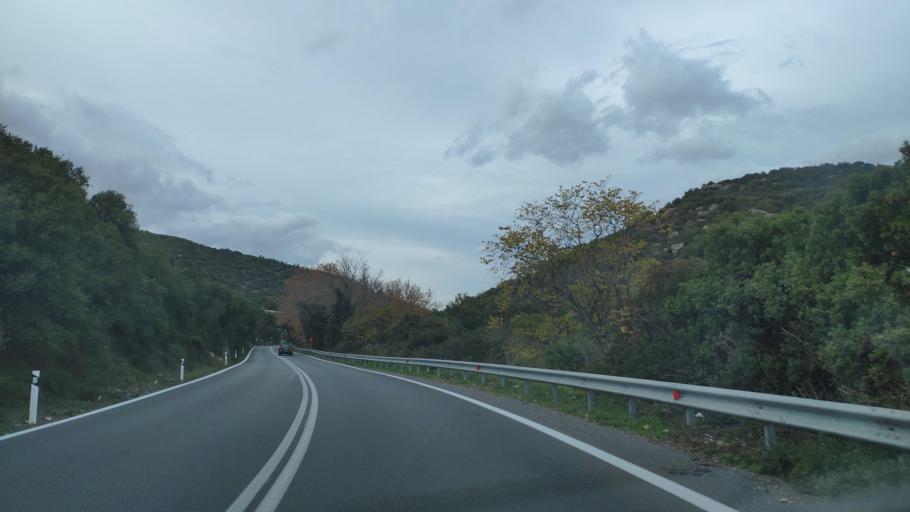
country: GR
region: Peloponnese
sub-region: Nomos Korinthias
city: Ayios Vasilios
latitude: 37.7647
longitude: 22.7298
